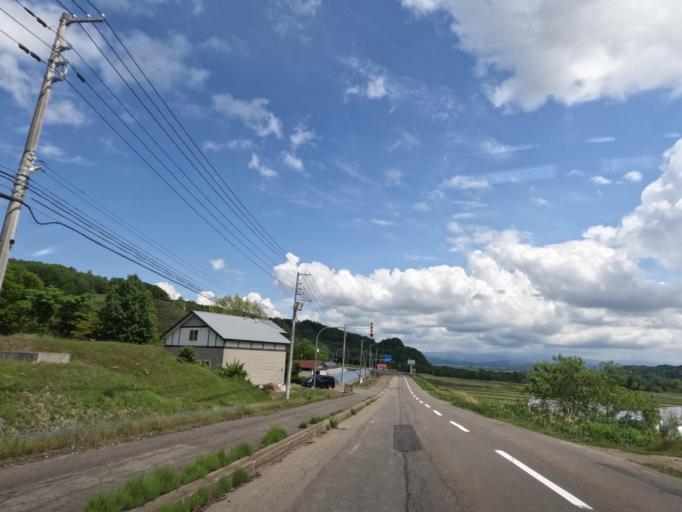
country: JP
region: Hokkaido
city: Takikawa
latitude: 43.5803
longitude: 141.8251
